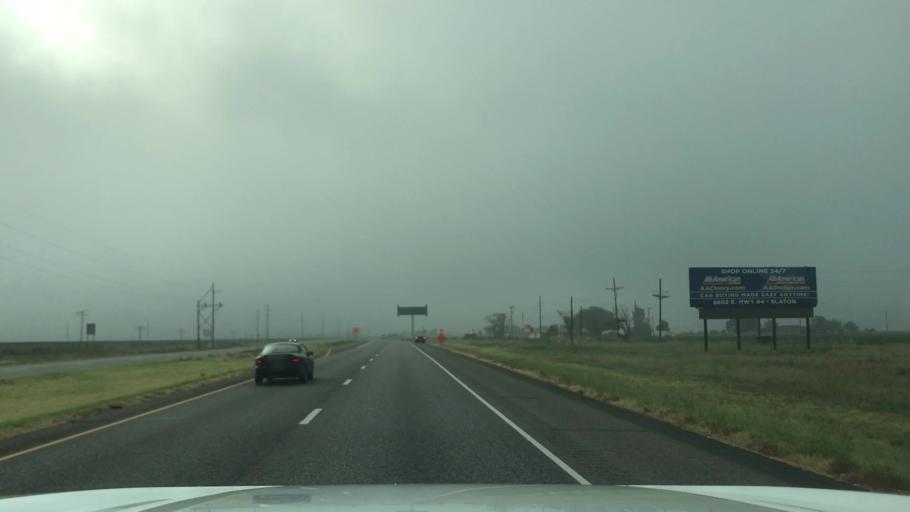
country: US
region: Texas
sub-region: Lubbock County
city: Slaton
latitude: 33.4637
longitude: -101.6771
